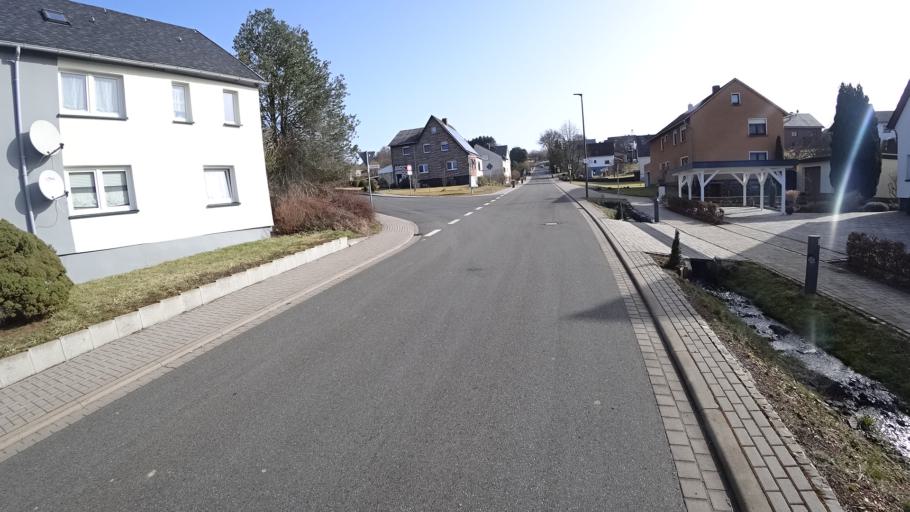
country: DE
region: Rheinland-Pfalz
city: Luckenbach
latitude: 50.7041
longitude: 7.8351
